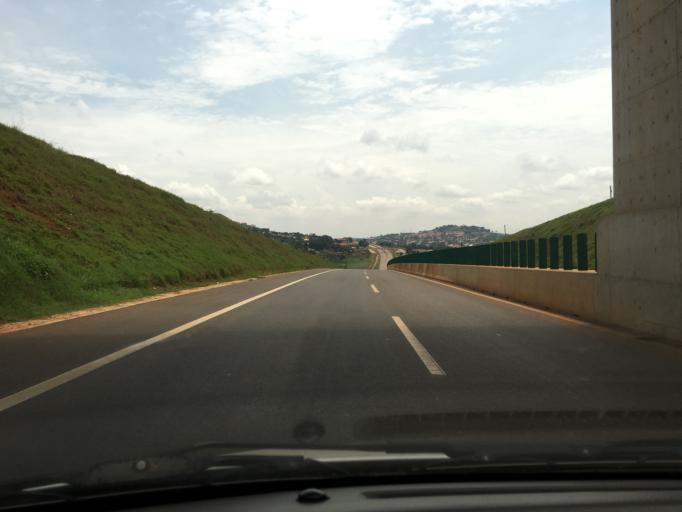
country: UG
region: Central Region
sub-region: Wakiso District
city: Kajansi
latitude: 0.1759
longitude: 32.5172
